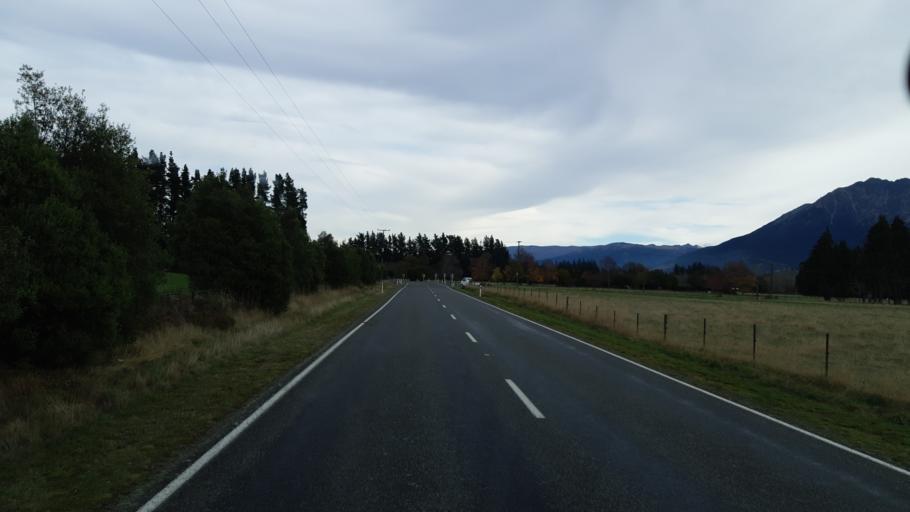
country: NZ
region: Tasman
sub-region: Tasman District
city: Brightwater
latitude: -41.6283
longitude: 173.3374
